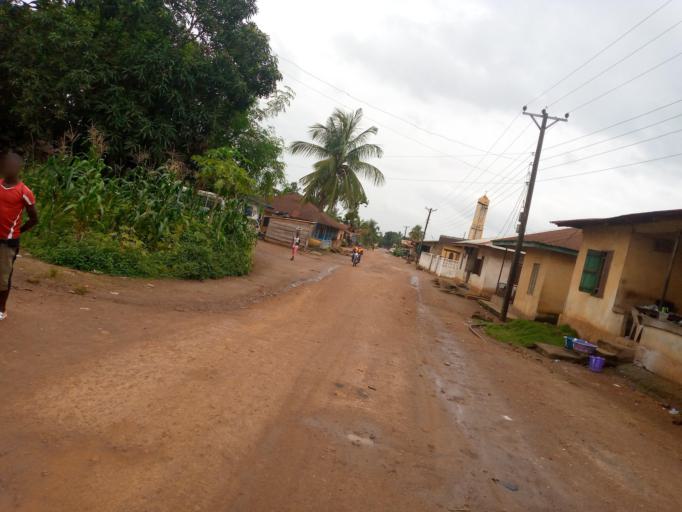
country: SL
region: Eastern Province
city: Kenema
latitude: 7.8849
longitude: -11.1810
